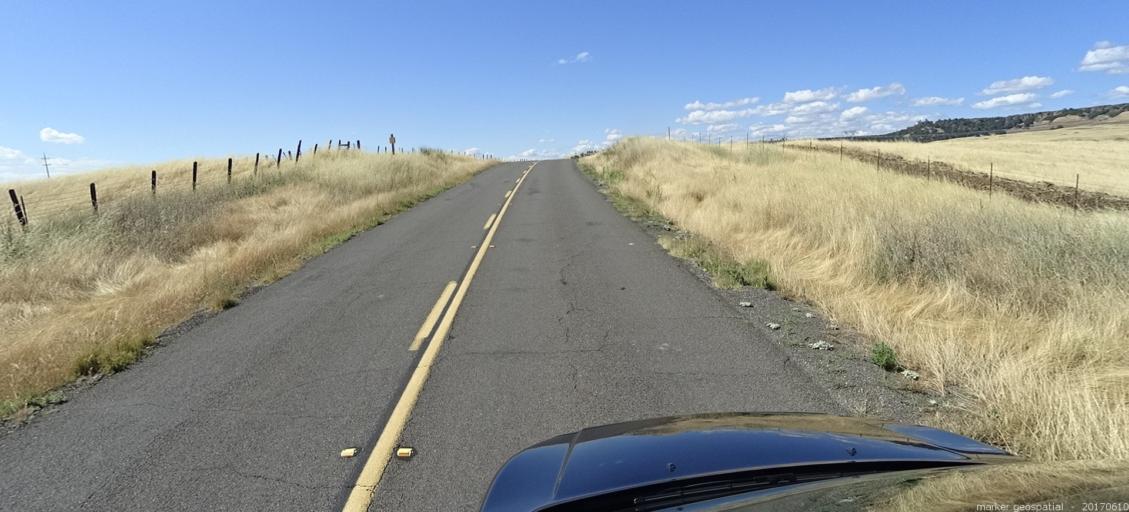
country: US
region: California
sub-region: Butte County
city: Thermalito
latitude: 39.5524
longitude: -121.5951
